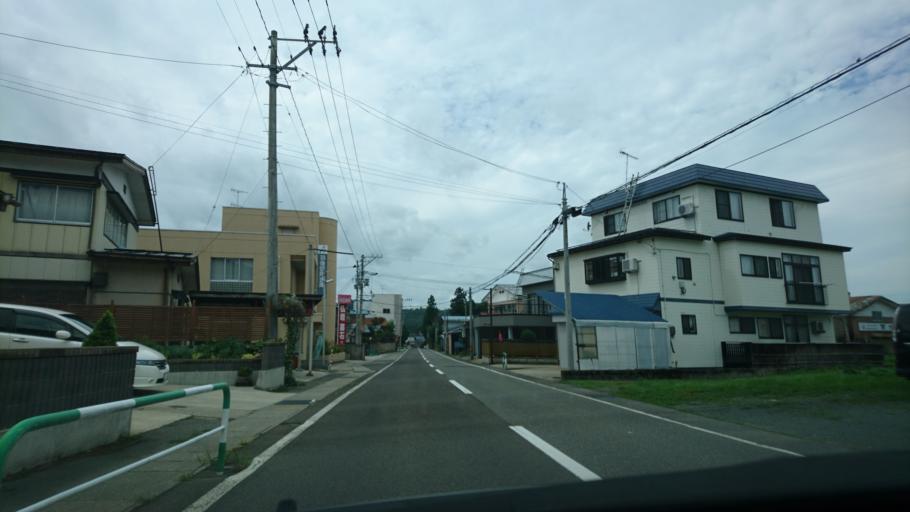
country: JP
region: Akita
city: Yuzawa
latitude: 39.1523
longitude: 140.5655
